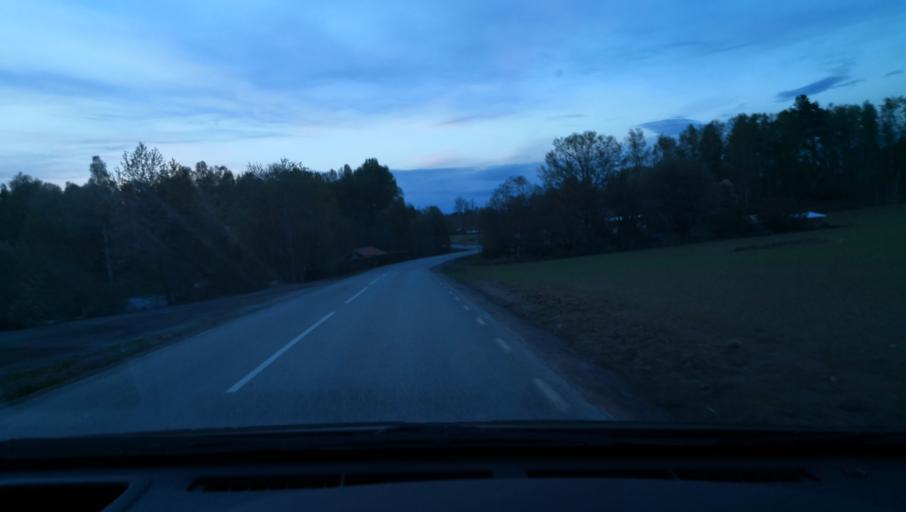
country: SE
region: OErebro
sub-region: Askersunds Kommun
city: Askersund
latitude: 58.9980
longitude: 14.8968
